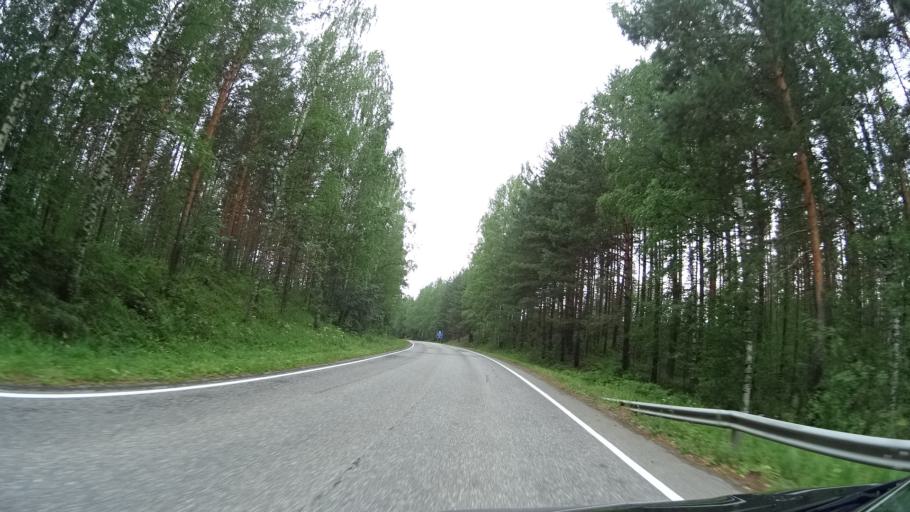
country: FI
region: Southern Savonia
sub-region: Savonlinna
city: Punkaharju
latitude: 61.7582
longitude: 29.4035
